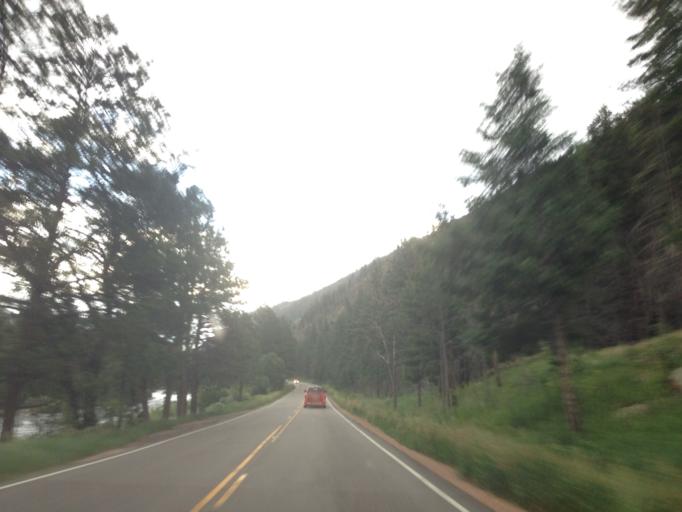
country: US
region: Colorado
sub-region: Larimer County
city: Laporte
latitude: 40.6877
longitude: -105.3581
